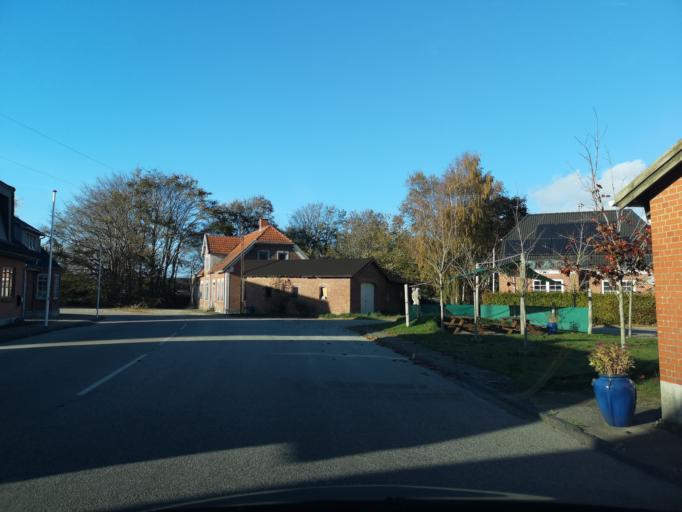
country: DK
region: Central Jutland
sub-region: Ringkobing-Skjern Kommune
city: Tarm
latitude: 55.8229
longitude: 8.4094
